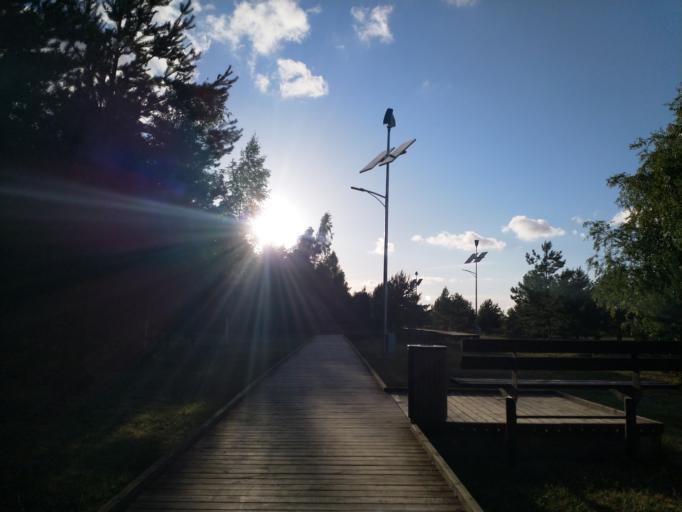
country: LV
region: Rojas
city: Roja
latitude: 57.5106
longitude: 22.7996
